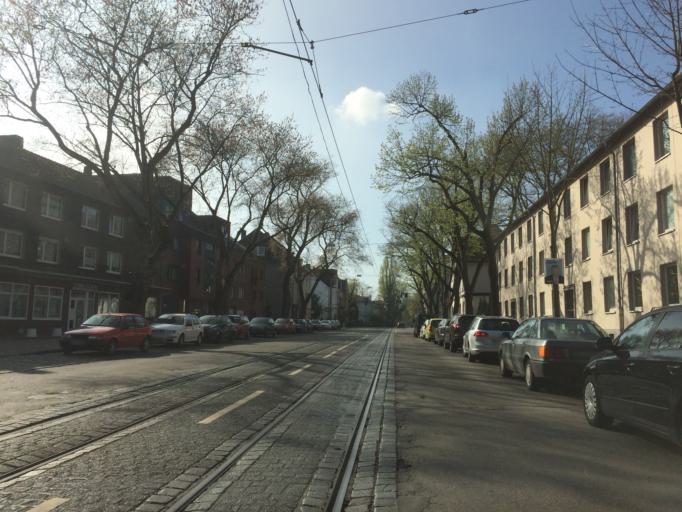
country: DE
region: North Rhine-Westphalia
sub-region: Regierungsbezirk Munster
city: Gelsenkirchen
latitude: 51.4940
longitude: 7.1204
